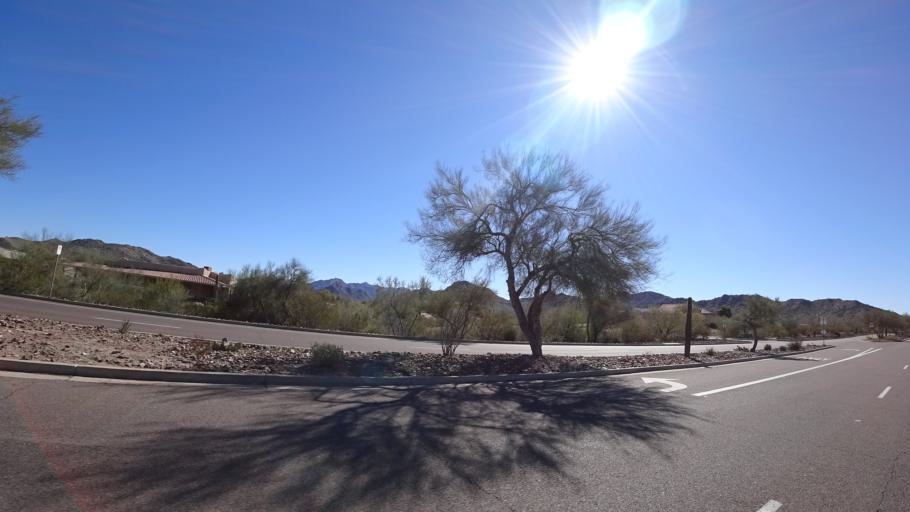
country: US
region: Arizona
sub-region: Maricopa County
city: Goodyear
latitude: 33.3687
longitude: -112.4034
